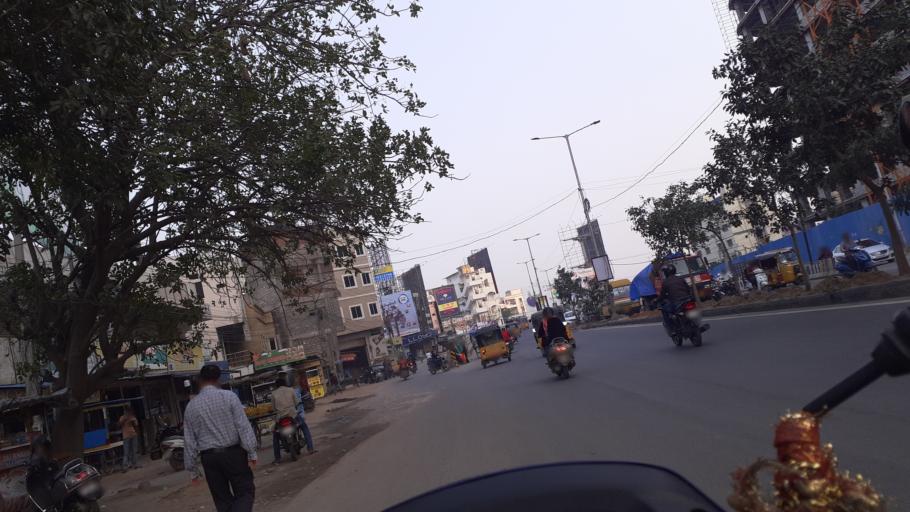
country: IN
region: Telangana
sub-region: Rangareddi
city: Kukatpalli
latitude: 17.4858
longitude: 78.3589
